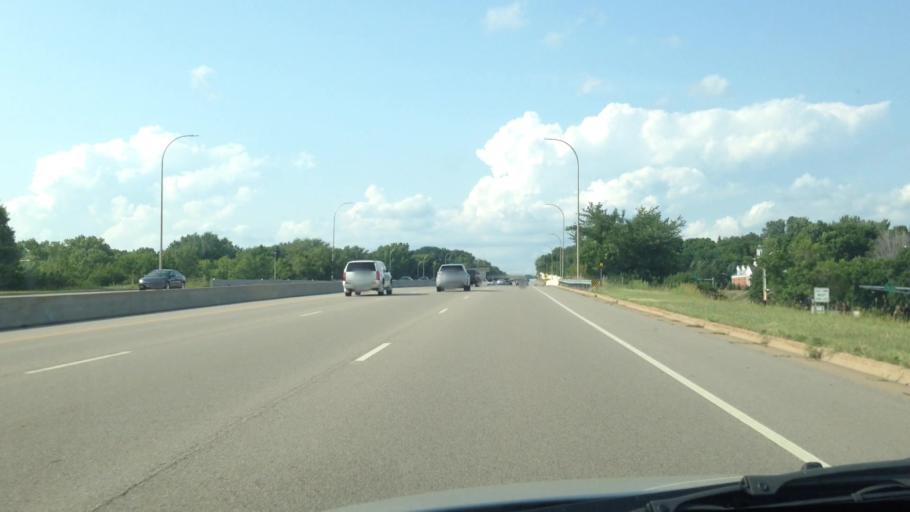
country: US
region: Minnesota
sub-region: Hennepin County
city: Edina
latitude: 44.8749
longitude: -93.3501
